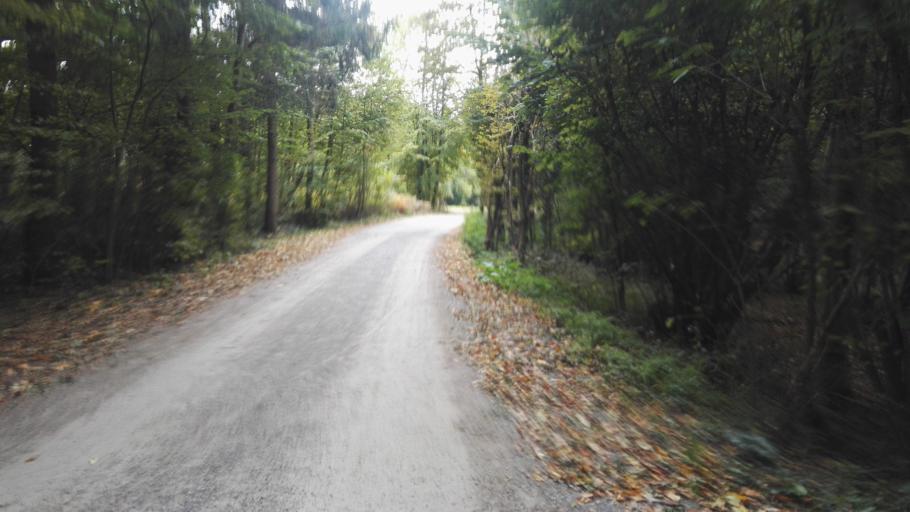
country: AT
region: Styria
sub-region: Graz Stadt
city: Mariatrost
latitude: 47.1022
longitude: 15.4960
